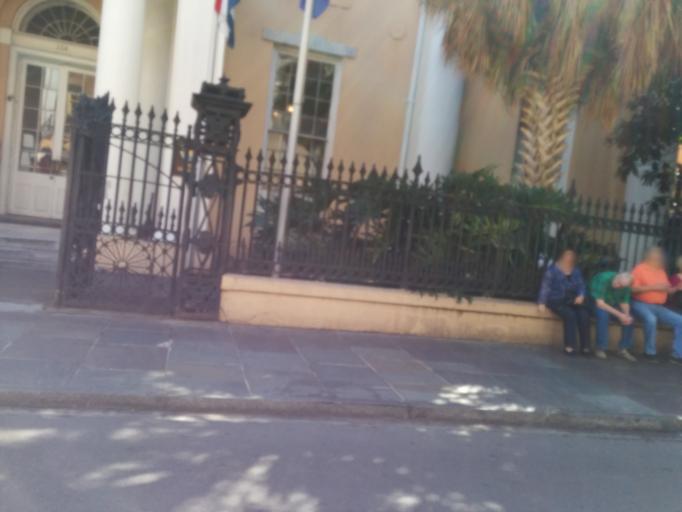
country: US
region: Louisiana
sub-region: Orleans Parish
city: New Orleans
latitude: 29.9555
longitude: -90.0671
